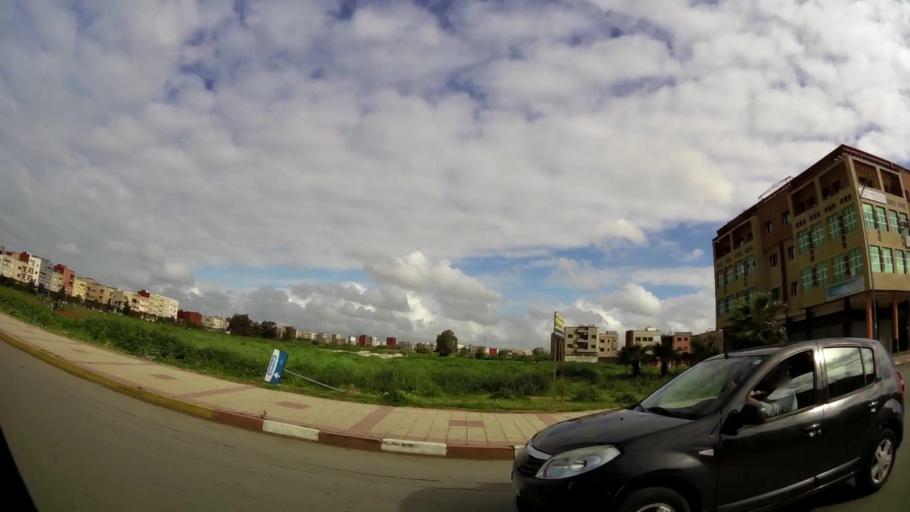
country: MA
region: Grand Casablanca
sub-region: Mohammedia
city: Mohammedia
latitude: 33.6982
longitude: -7.3648
